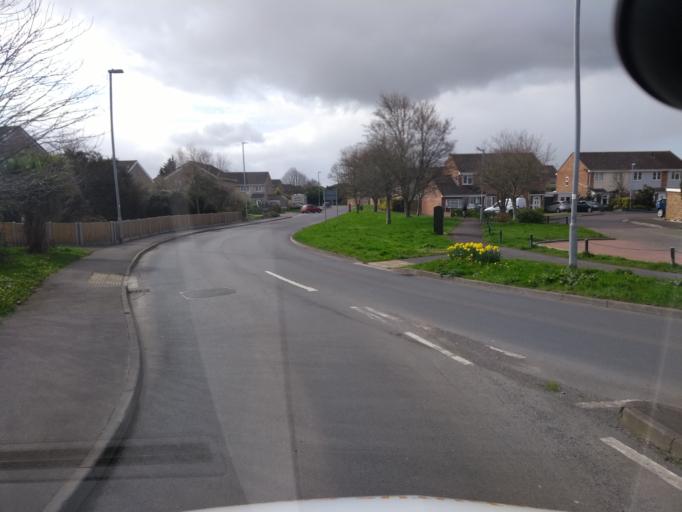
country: GB
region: England
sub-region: Somerset
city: Puriton
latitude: 51.1398
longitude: -2.9757
